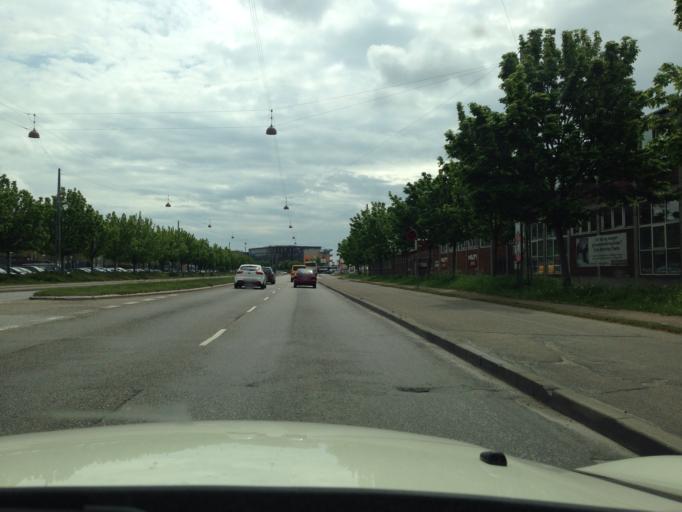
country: DK
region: Capital Region
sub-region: Frederiksberg Kommune
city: Frederiksberg
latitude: 55.6487
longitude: 12.5411
